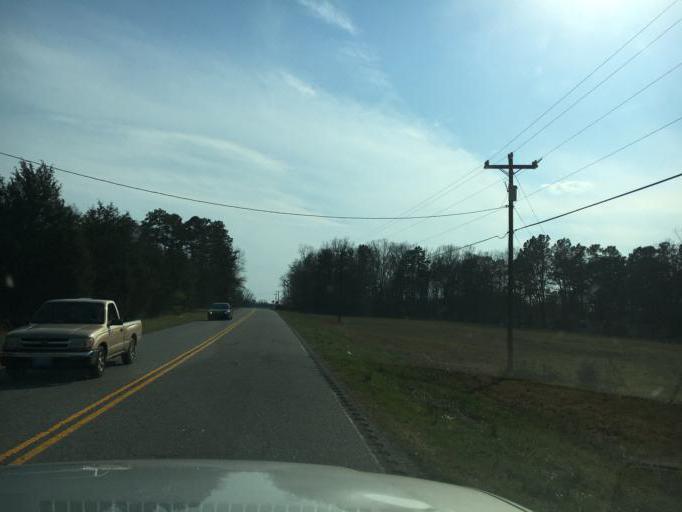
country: US
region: South Carolina
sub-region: Spartanburg County
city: Mayo
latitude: 35.1586
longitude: -81.8492
